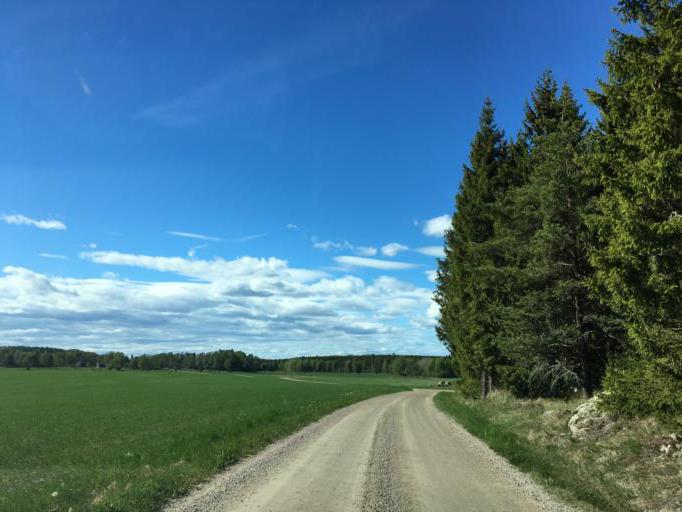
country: SE
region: Soedermanland
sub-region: Eskilstuna Kommun
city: Kvicksund
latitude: 59.3761
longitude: 16.2629
